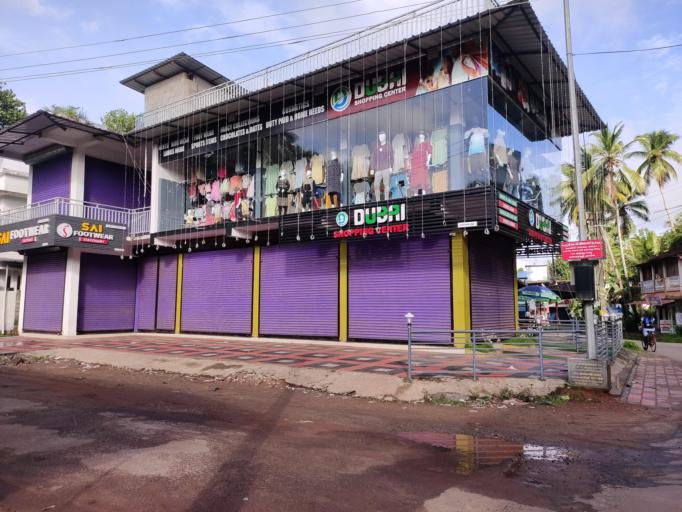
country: IN
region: Kerala
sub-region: Palakkad district
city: Mannarakkat
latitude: 10.9318
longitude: 76.4907
